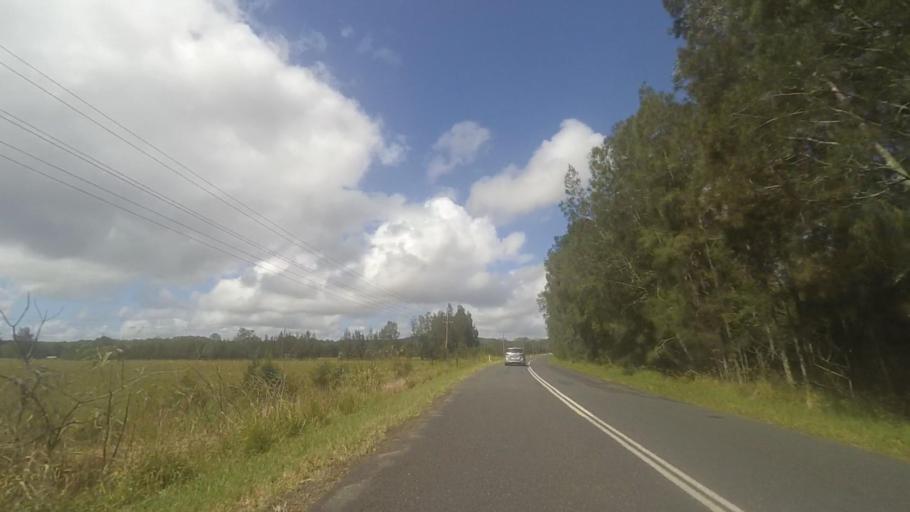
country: AU
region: New South Wales
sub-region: Great Lakes
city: Bulahdelah
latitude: -32.3914
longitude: 152.3281
